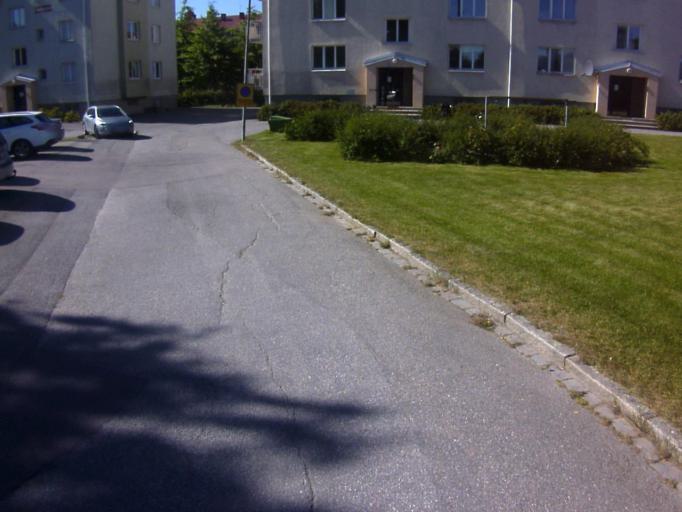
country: SE
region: Soedermanland
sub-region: Eskilstuna Kommun
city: Eskilstuna
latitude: 59.3780
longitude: 16.5230
